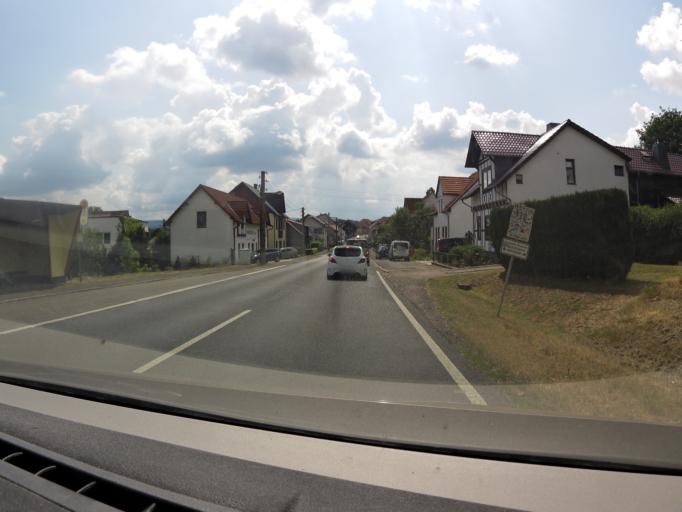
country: DE
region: Thuringia
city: Plaue
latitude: 50.7817
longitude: 10.9013
